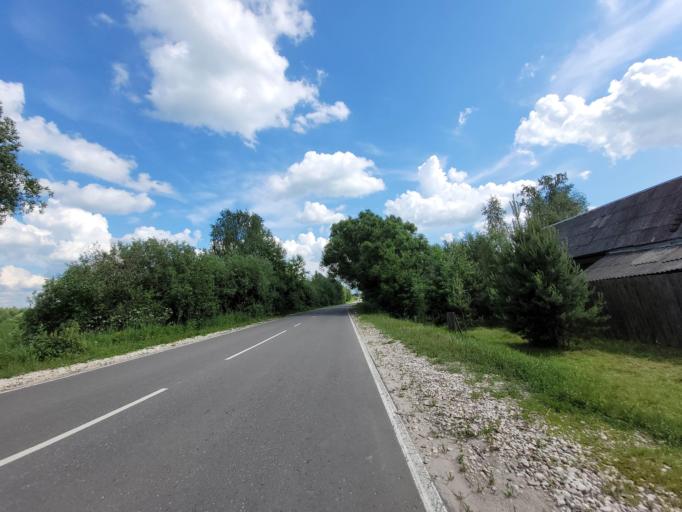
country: RU
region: Moskovskaya
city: Konobeyevo
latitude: 55.3982
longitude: 38.6807
